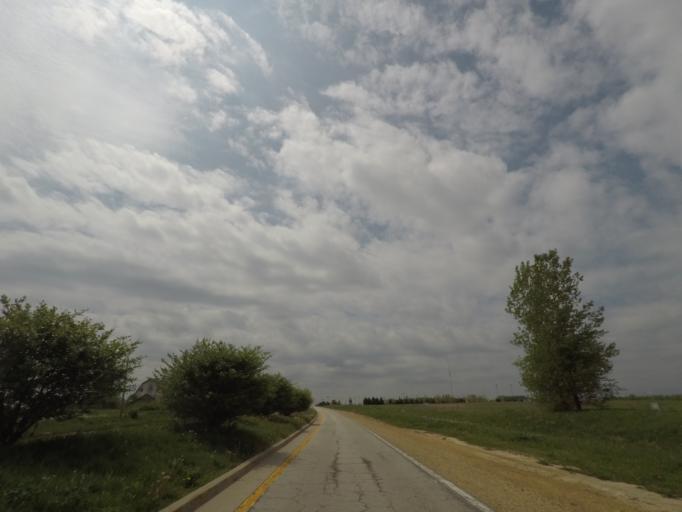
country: US
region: Illinois
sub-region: Winnebago County
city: Machesney Park
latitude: 42.3292
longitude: -88.9503
